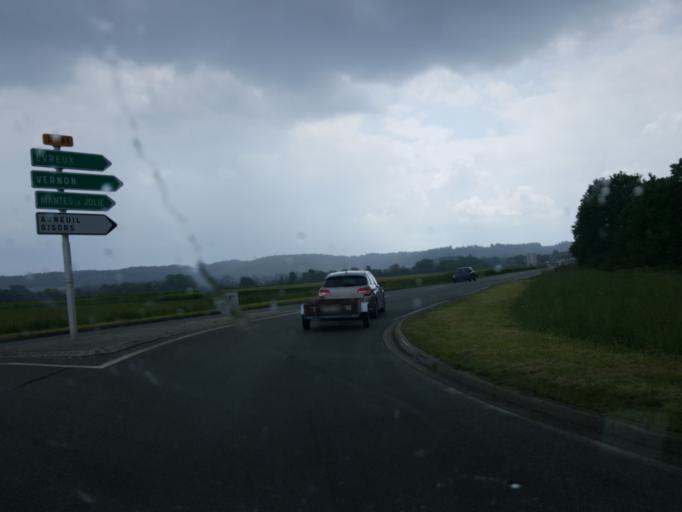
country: FR
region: Picardie
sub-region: Departement de l'Oise
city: Auneuil
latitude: 49.3892
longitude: 2.0067
